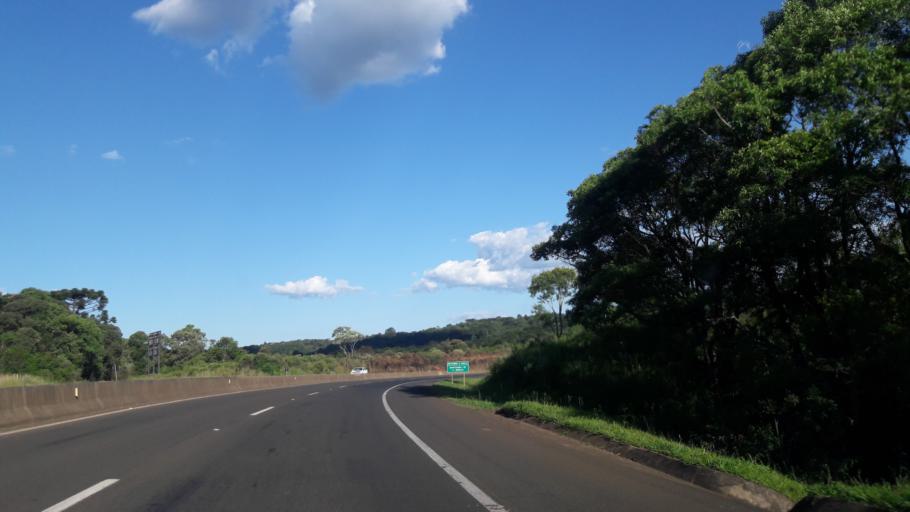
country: BR
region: Parana
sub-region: Guarapuava
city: Guarapuava
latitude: -25.3396
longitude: -51.4168
